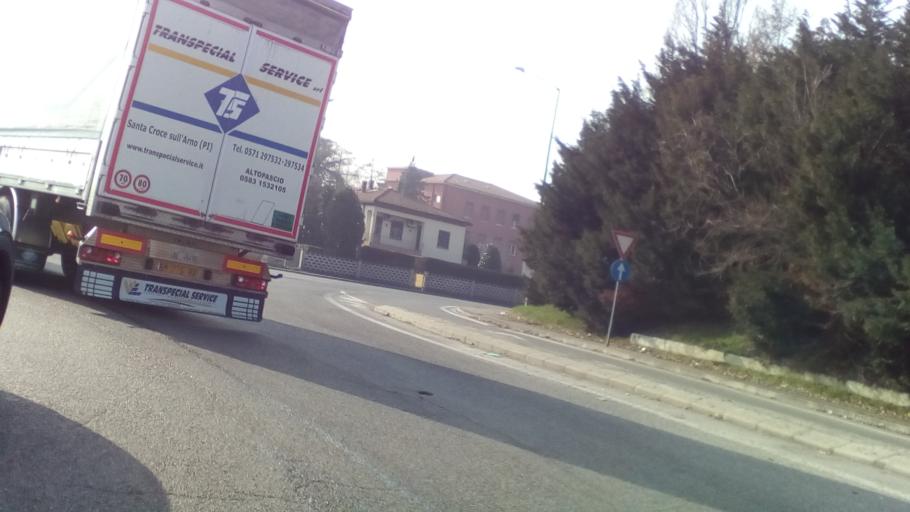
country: IT
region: Emilia-Romagna
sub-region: Provincia di Modena
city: Modena
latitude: 44.6257
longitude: 10.9508
